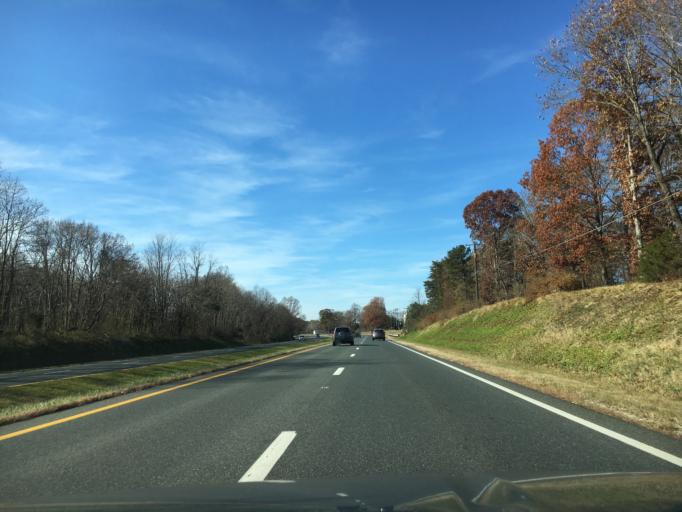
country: US
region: Virginia
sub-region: Campbell County
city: Concord
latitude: 37.3503
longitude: -78.9420
